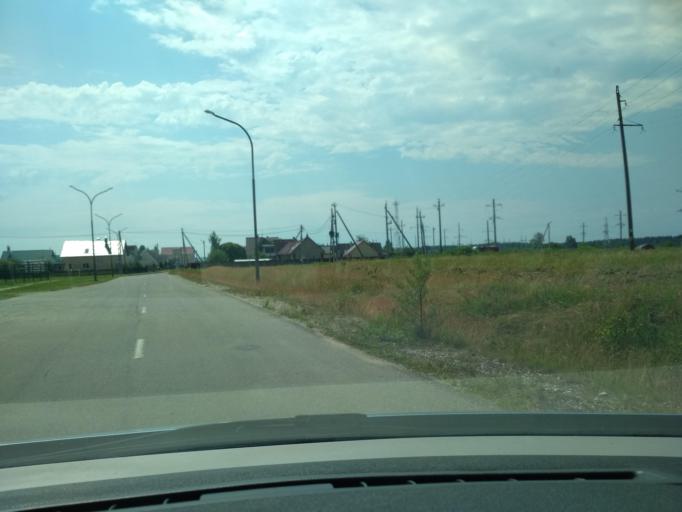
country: BY
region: Grodnenskaya
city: Astravyets
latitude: 54.6235
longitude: 25.9564
